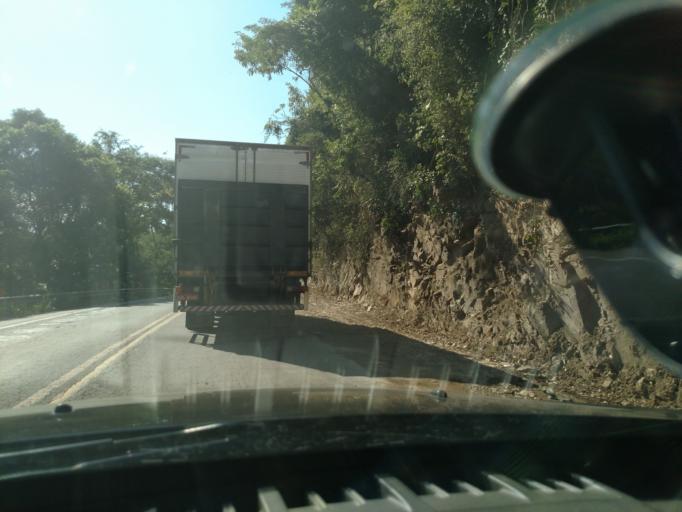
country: BR
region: Santa Catarina
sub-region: Ibirama
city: Ibirama
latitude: -27.0952
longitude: -49.4658
